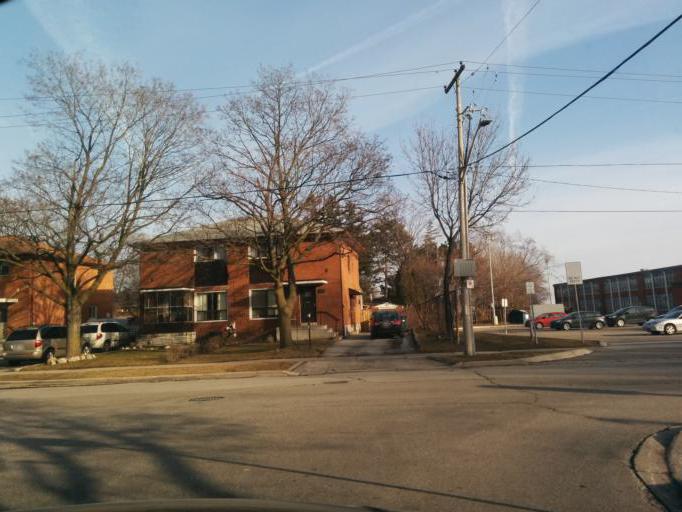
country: CA
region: Ontario
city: Etobicoke
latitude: 43.6089
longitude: -79.5970
